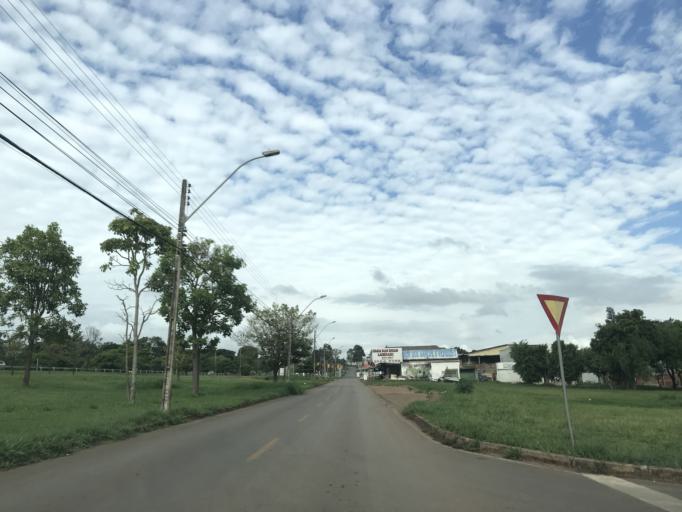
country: BR
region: Federal District
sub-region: Brasilia
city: Brasilia
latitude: -15.6591
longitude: -47.7925
